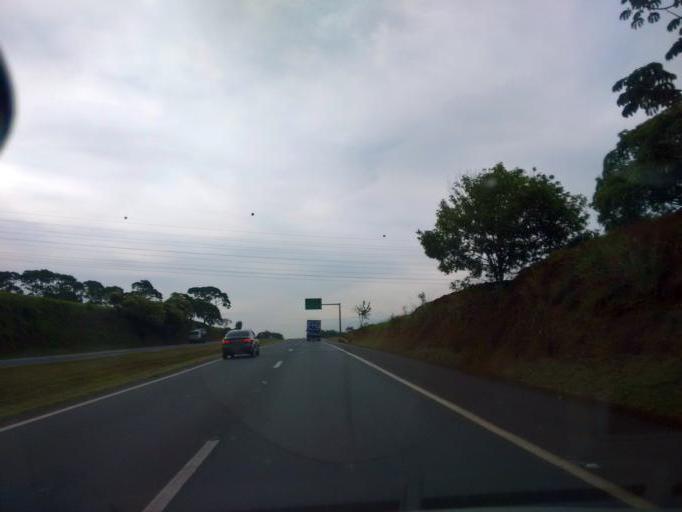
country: BR
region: Sao Paulo
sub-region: Araraquara
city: Araraquara
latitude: -21.7917
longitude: -48.2145
